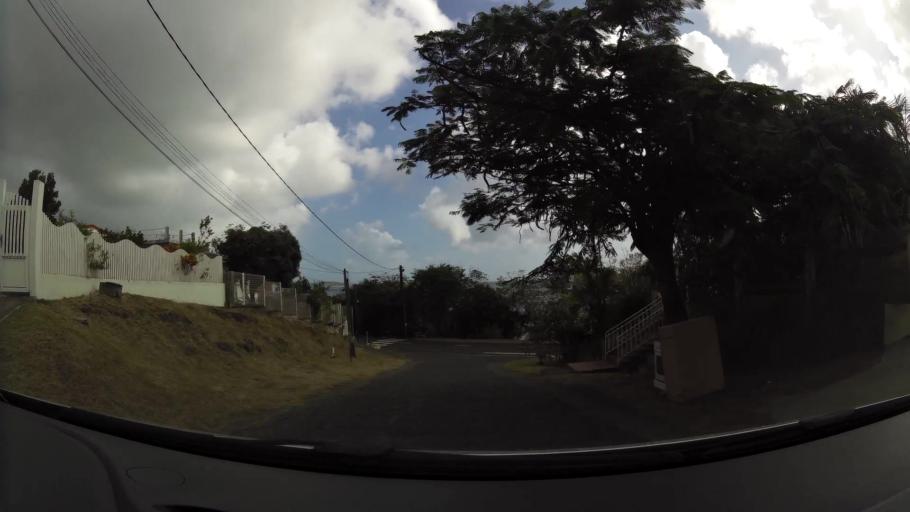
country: MQ
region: Martinique
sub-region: Martinique
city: Sainte-Luce
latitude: 14.4667
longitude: -60.9254
